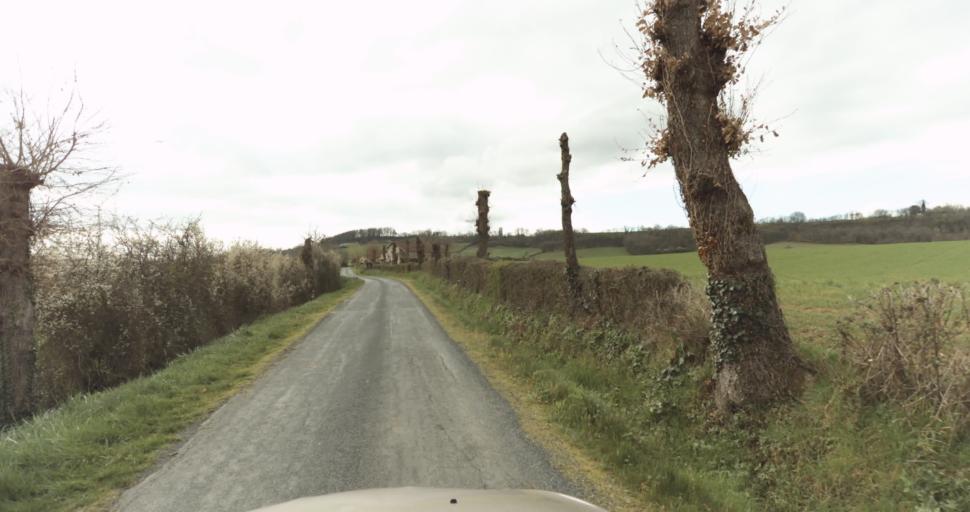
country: FR
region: Midi-Pyrenees
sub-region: Departement du Tarn
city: Frejairolles
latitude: 43.8743
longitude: 2.2039
